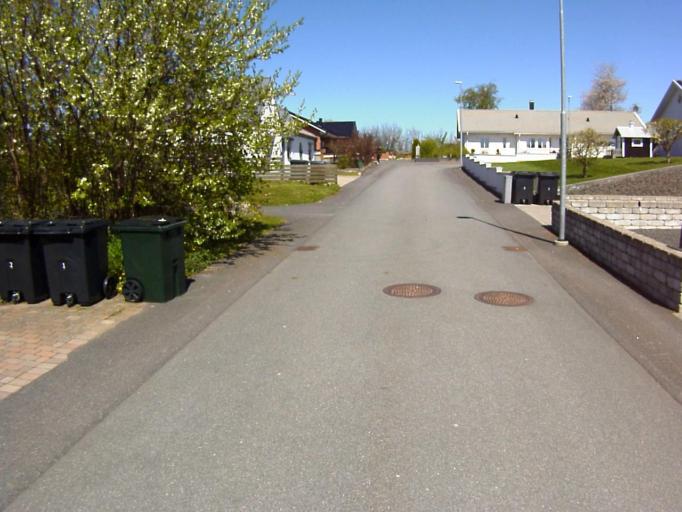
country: SE
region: Skane
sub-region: Kristianstads Kommun
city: Fjalkinge
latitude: 56.0490
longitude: 14.2170
